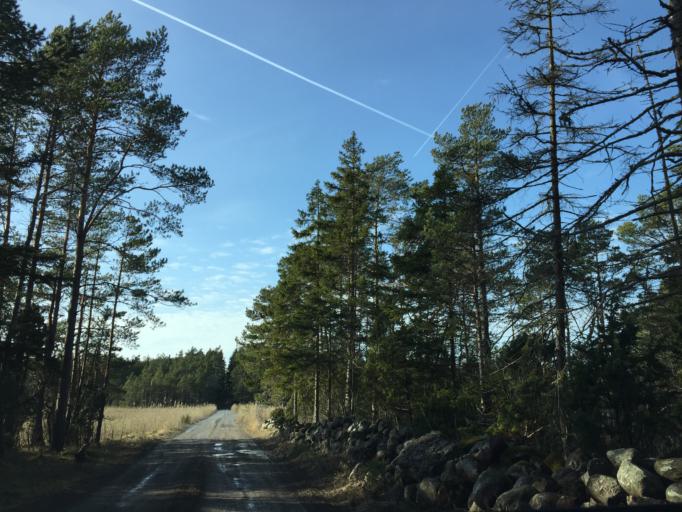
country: EE
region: Saare
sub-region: Kuressaare linn
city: Kuressaare
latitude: 58.3774
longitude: 22.0073
